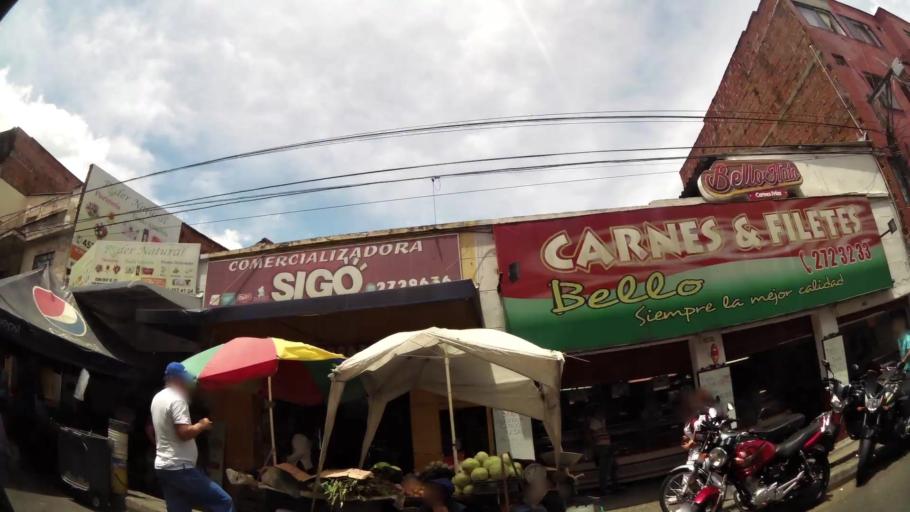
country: CO
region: Antioquia
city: Bello
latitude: 6.3351
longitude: -75.5564
